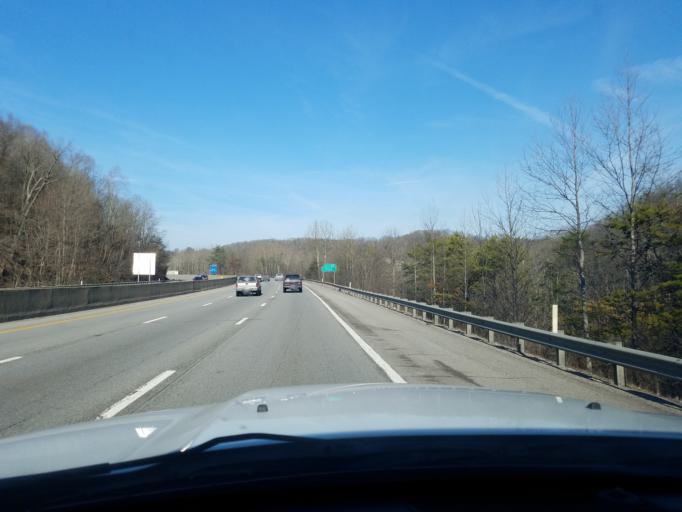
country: US
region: West Virginia
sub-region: Kanawha County
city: Cross Lanes
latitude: 38.4255
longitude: -81.8112
